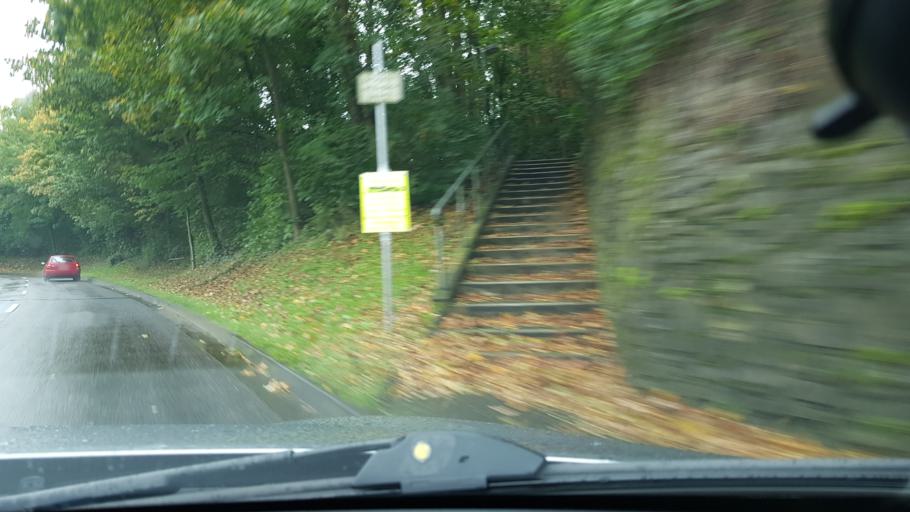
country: DE
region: Rheinland-Pfalz
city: Vallendar
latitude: 50.3877
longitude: 7.6216
